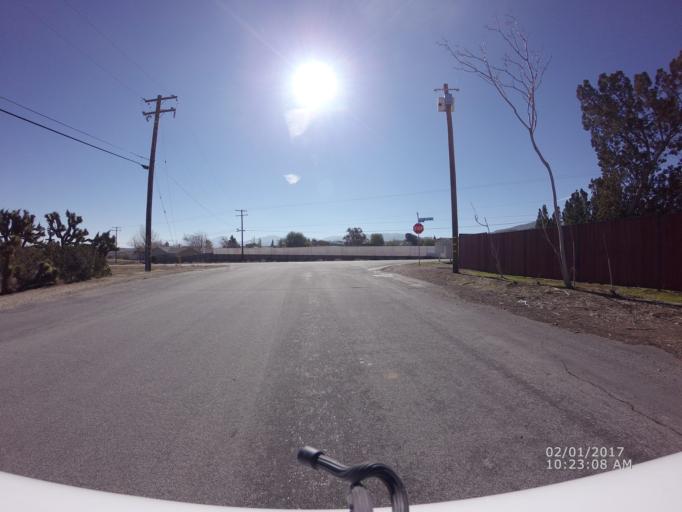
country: US
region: California
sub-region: Los Angeles County
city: Palmdale
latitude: 34.5424
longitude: -118.1129
